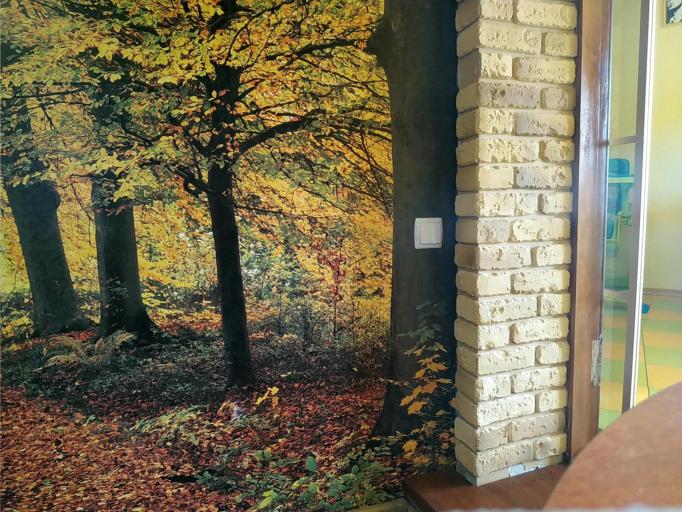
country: RU
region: Smolensk
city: Katyn'
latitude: 54.9404
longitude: 31.7248
